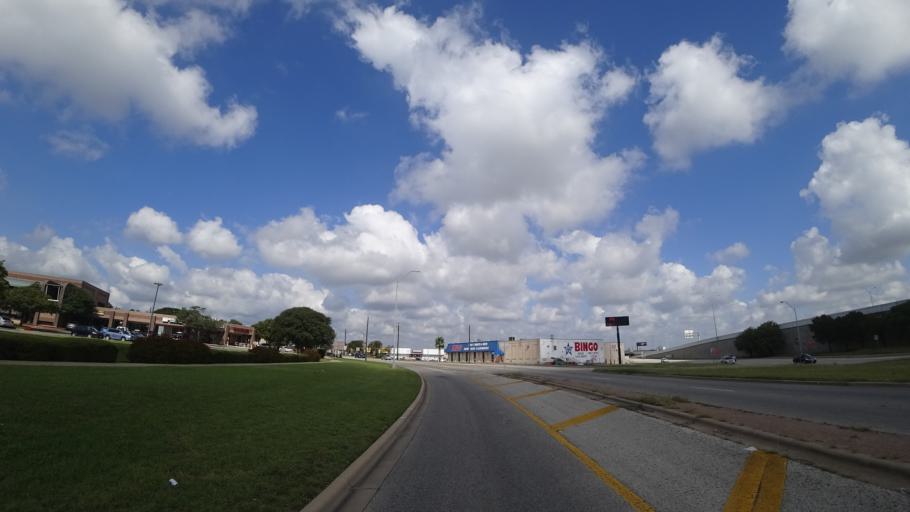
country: US
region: Texas
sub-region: Travis County
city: Austin
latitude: 30.3476
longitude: -97.7138
